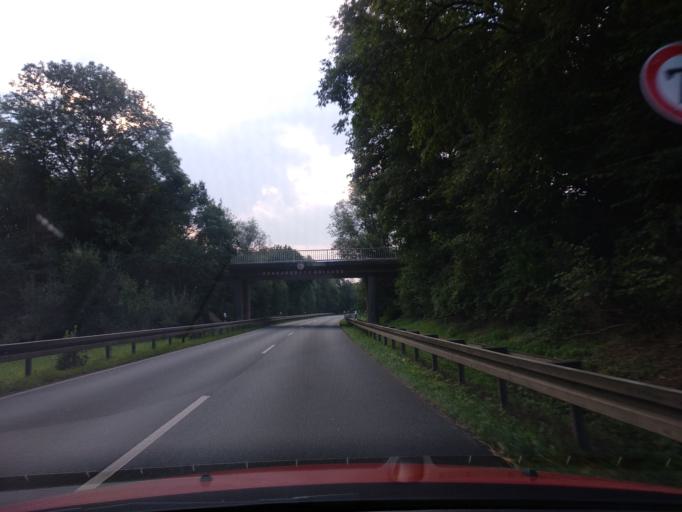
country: DE
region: Hesse
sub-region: Regierungsbezirk Kassel
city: Calden
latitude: 51.3701
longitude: 9.3963
